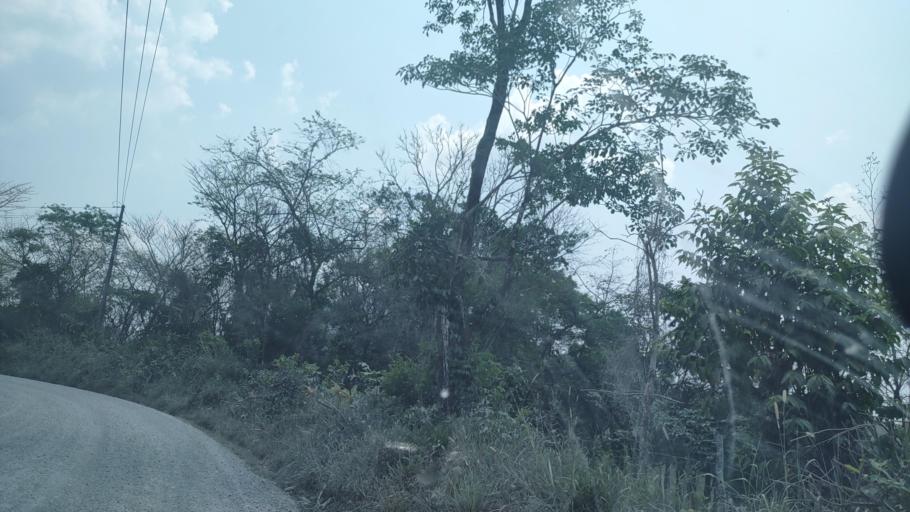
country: MX
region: Tabasco
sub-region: Huimanguillo
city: Francisco Rueda
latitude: 17.6115
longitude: -93.9133
